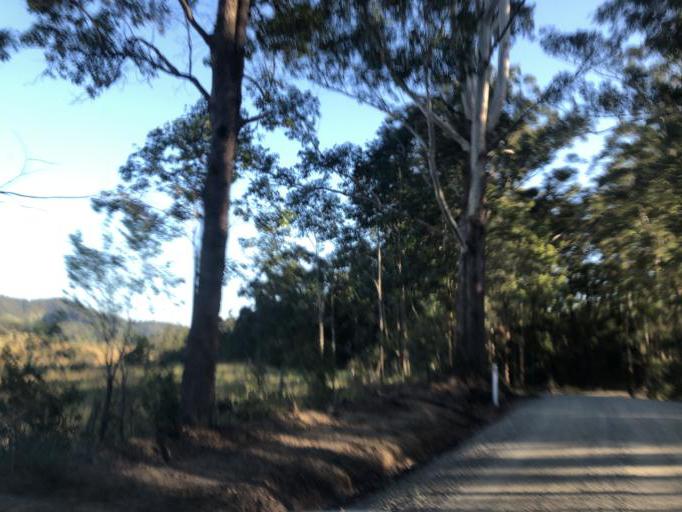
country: AU
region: New South Wales
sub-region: Nambucca Shire
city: Nambucca
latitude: -30.5843
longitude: 152.9351
